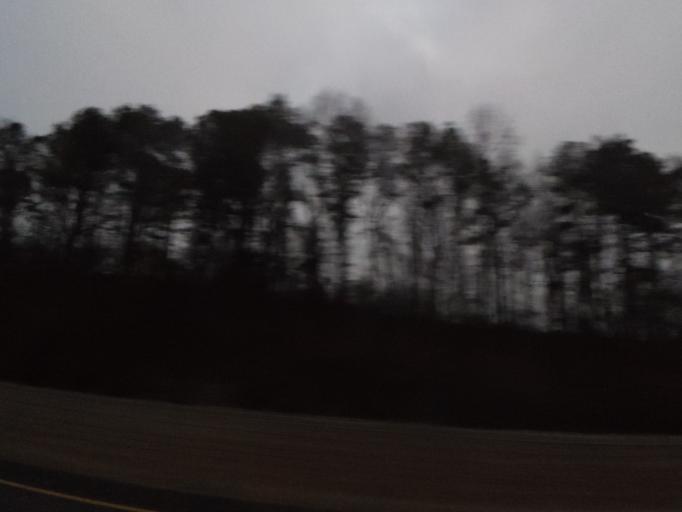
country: US
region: Alabama
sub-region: Morgan County
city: Falkville
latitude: 34.2867
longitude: -86.9077
